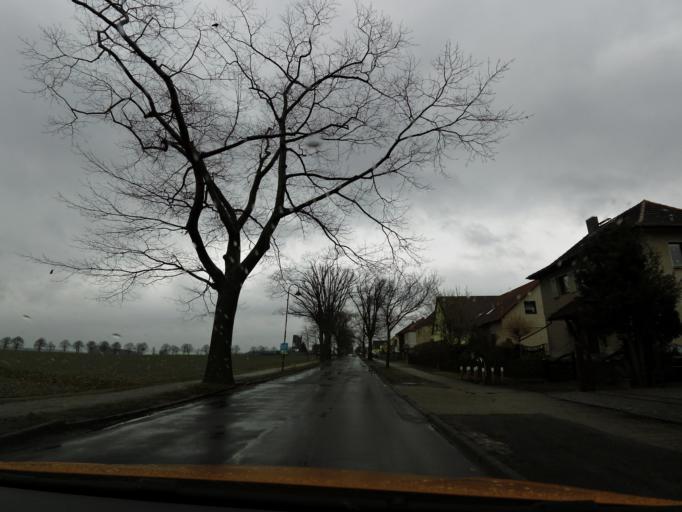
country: DE
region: Brandenburg
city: Rangsdorf
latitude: 52.3249
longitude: 13.4301
